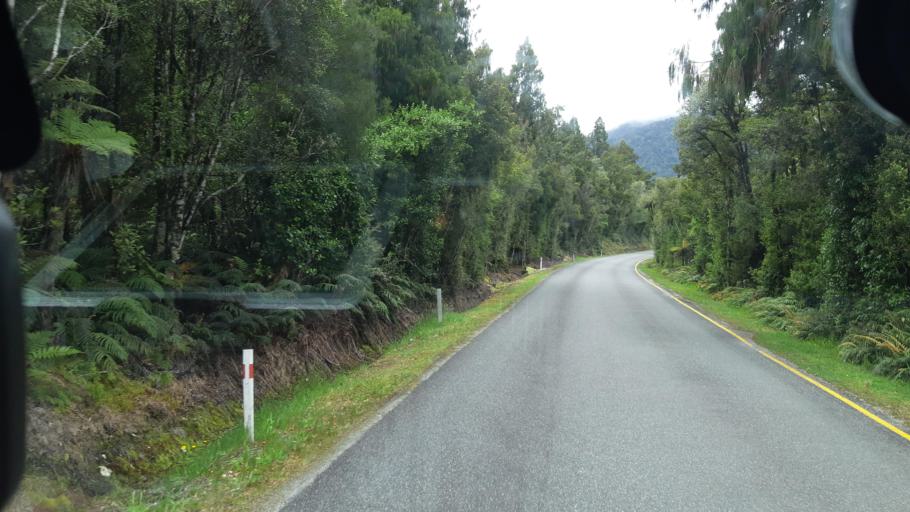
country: NZ
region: West Coast
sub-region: Westland District
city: Hokitika
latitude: -42.7988
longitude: 171.1416
